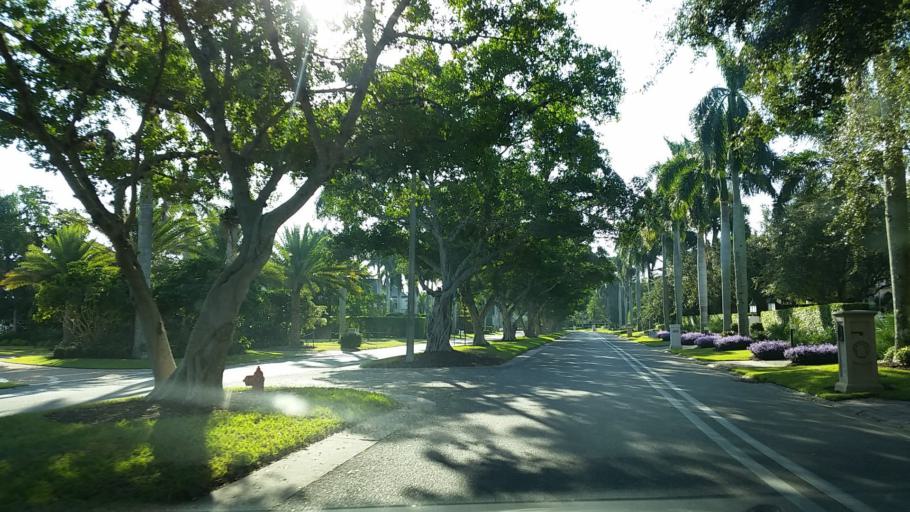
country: US
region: Florida
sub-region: Collier County
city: Naples
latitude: 26.1138
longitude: -81.7969
